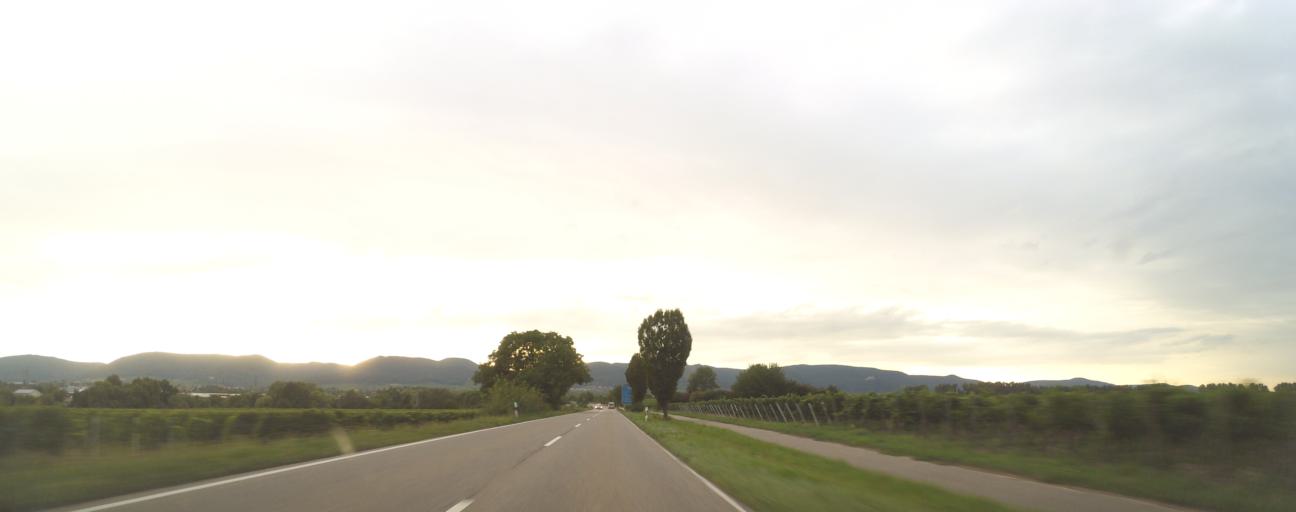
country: DE
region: Rheinland-Pfalz
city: Venningen
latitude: 49.2851
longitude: 8.1602
